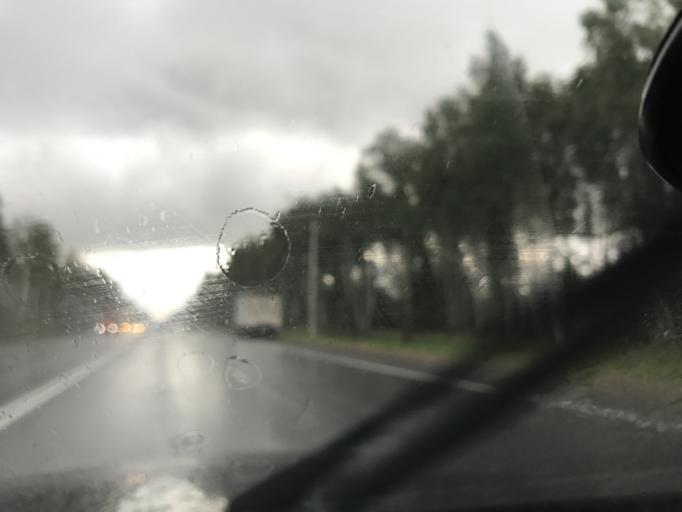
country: RU
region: Vladimir
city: Sobinka
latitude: 56.0349
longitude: 40.0284
